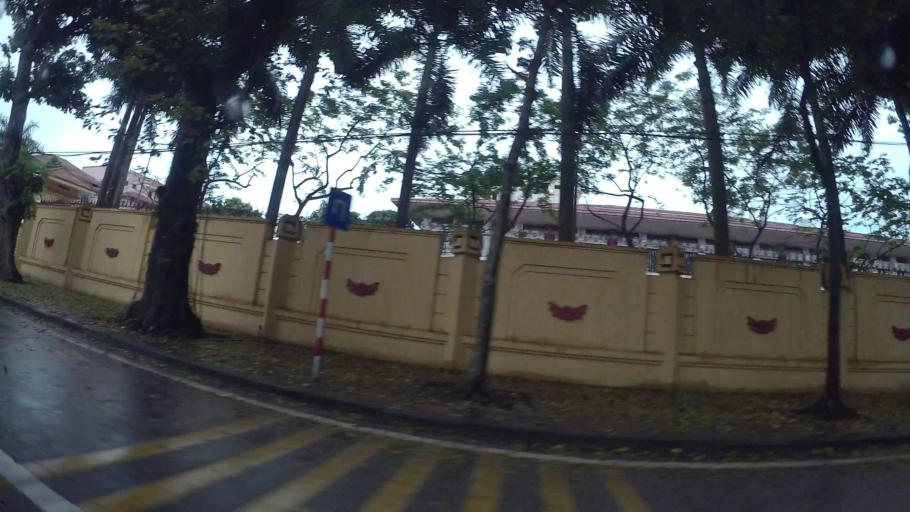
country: VN
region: Ha Noi
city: Hanoi
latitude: 21.0370
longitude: 105.8414
